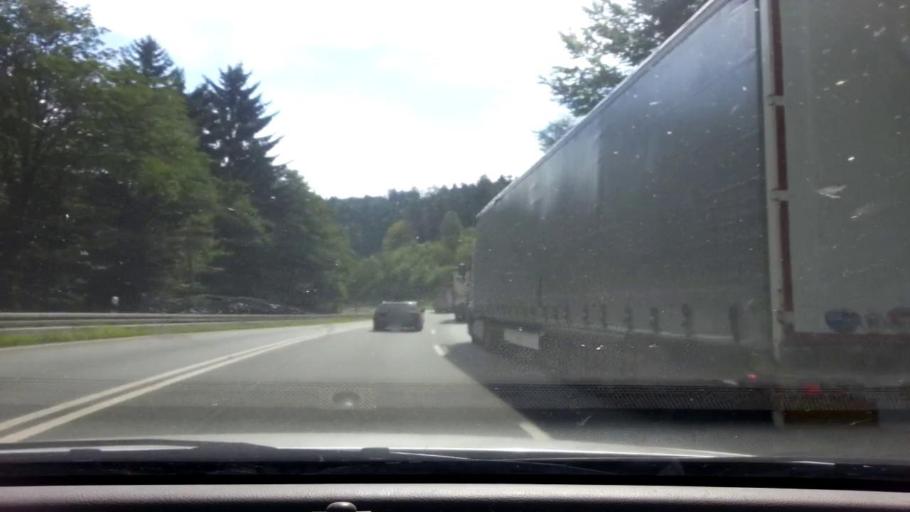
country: DE
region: Bavaria
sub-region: Upper Franconia
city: Bischofsgrun
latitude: 50.0426
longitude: 11.7318
